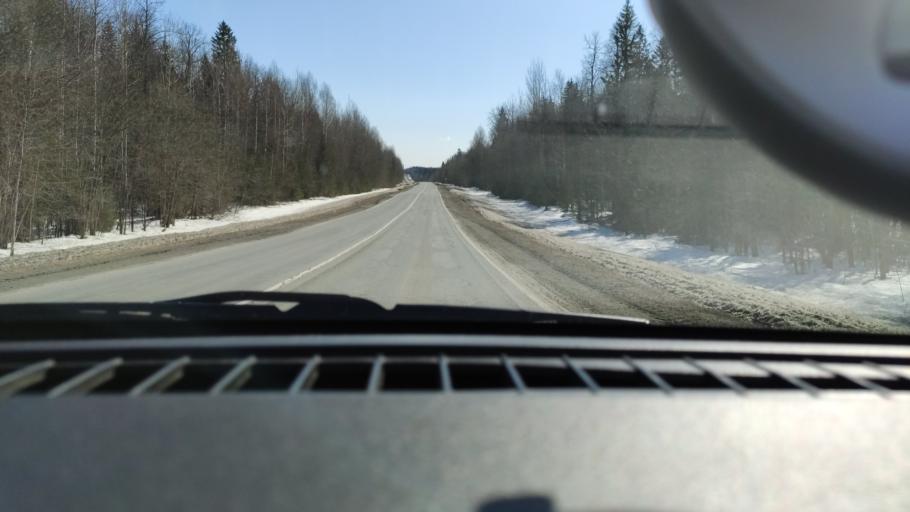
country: RU
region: Perm
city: Perm
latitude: 58.1727
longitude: 56.2329
